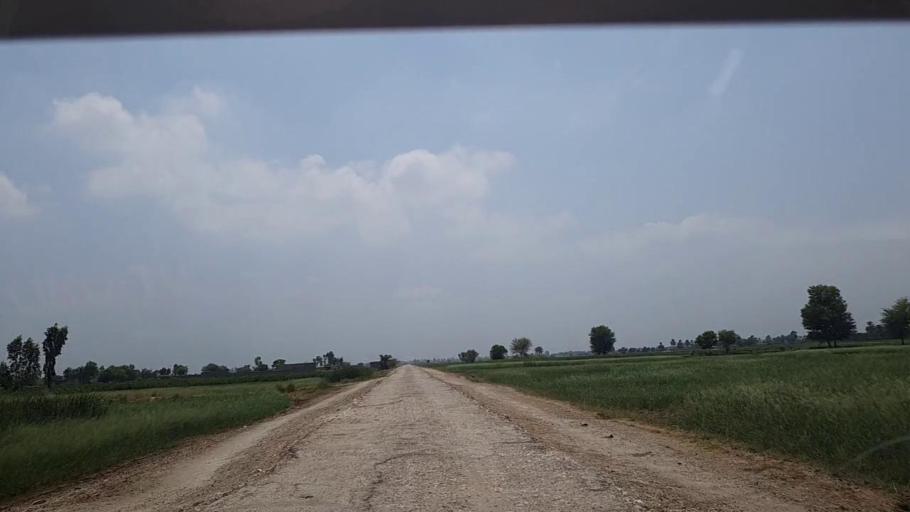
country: PK
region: Sindh
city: Khanpur
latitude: 27.9059
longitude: 69.3920
